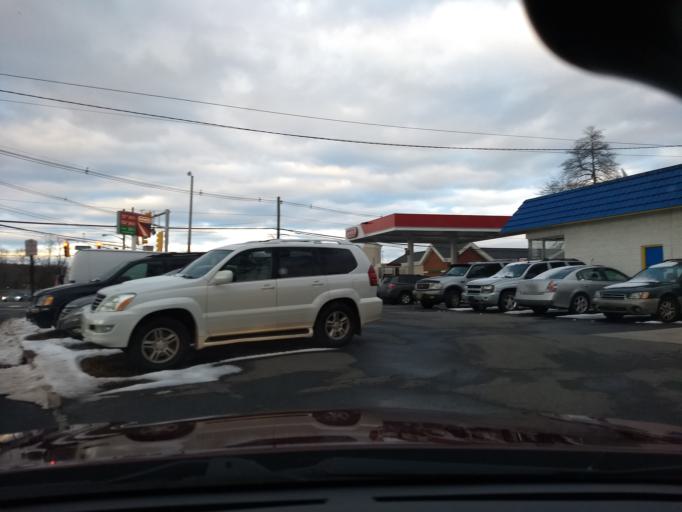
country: US
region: New Jersey
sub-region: Morris County
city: Morris Plains
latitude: 40.8113
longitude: -74.4697
